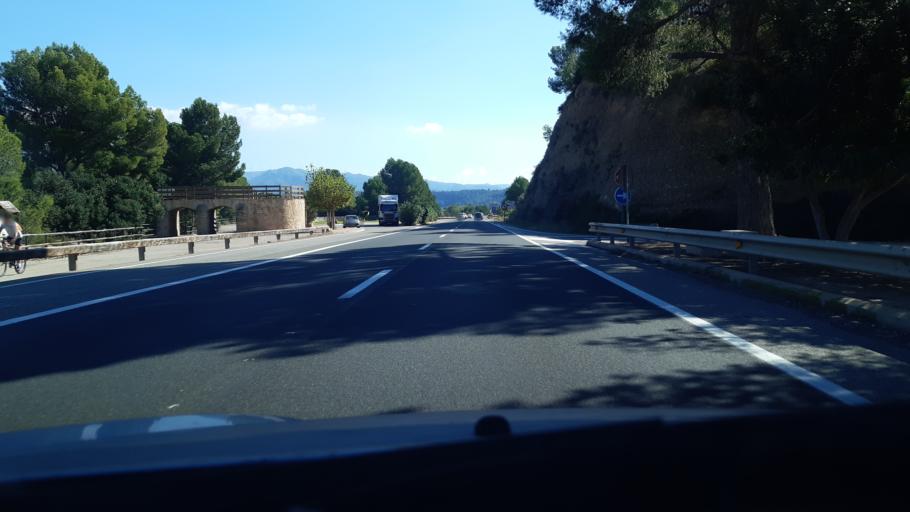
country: ES
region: Catalonia
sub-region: Provincia de Tarragona
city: Tivenys
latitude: 40.9212
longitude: 0.4911
